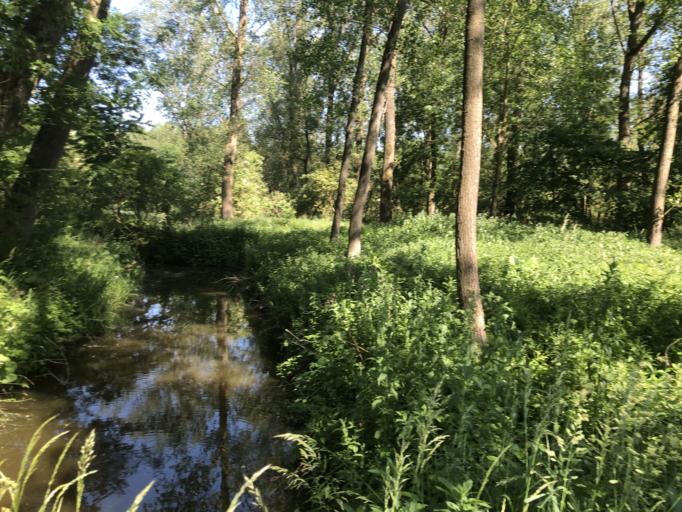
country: BE
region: Flanders
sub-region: Provincie Antwerpen
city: Bornem
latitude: 51.1232
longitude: 4.2466
